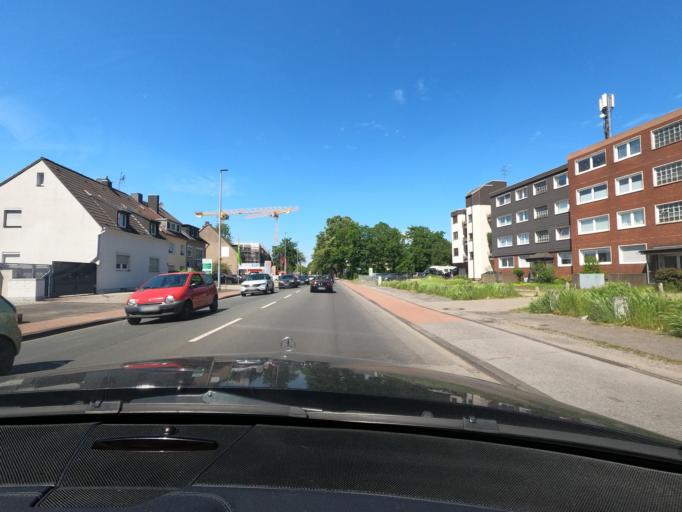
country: DE
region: North Rhine-Westphalia
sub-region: Regierungsbezirk Dusseldorf
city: Hochfeld
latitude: 51.3878
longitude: 6.7590
